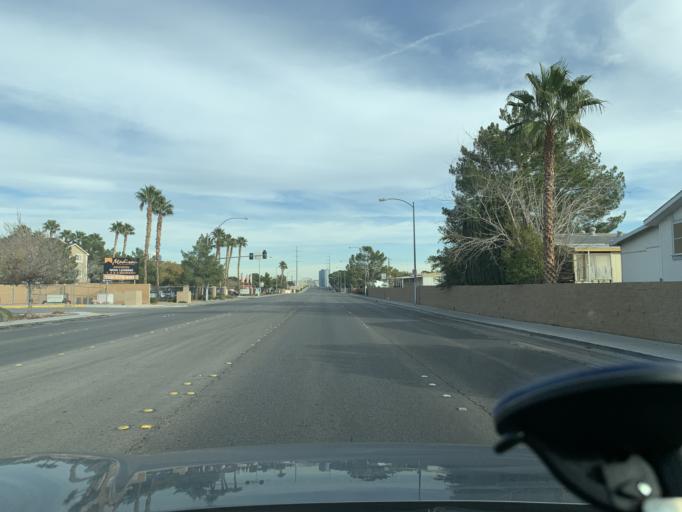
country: US
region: Nevada
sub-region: Clark County
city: Spring Valley
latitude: 36.1075
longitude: -115.2193
